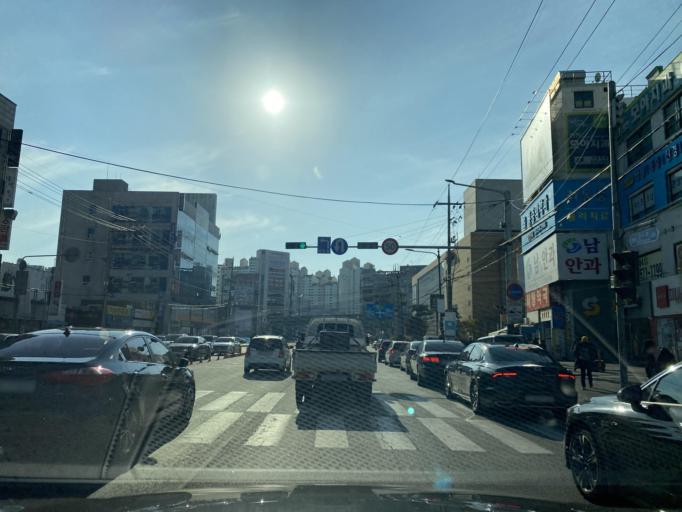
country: KR
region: Chungcheongnam-do
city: Cheonan
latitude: 36.7963
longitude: 127.1288
